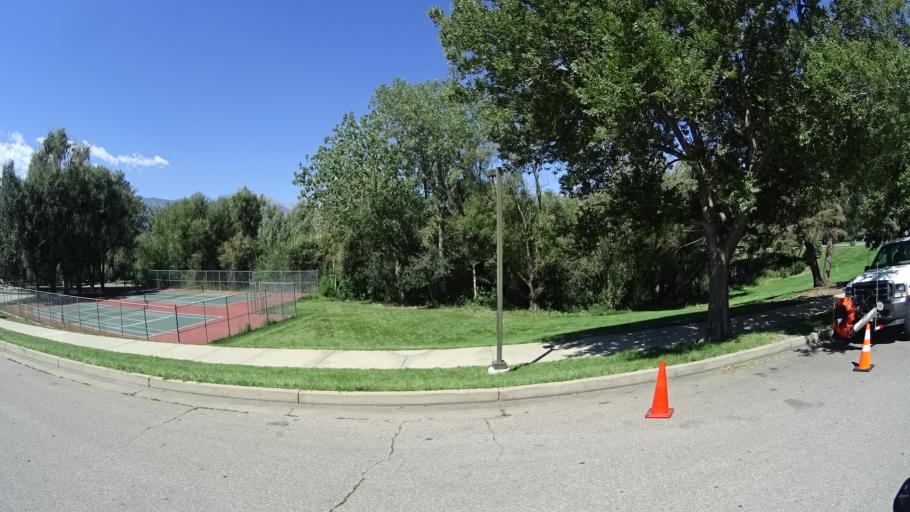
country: US
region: Colorado
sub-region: El Paso County
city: Colorado Springs
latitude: 38.8411
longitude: -104.8122
